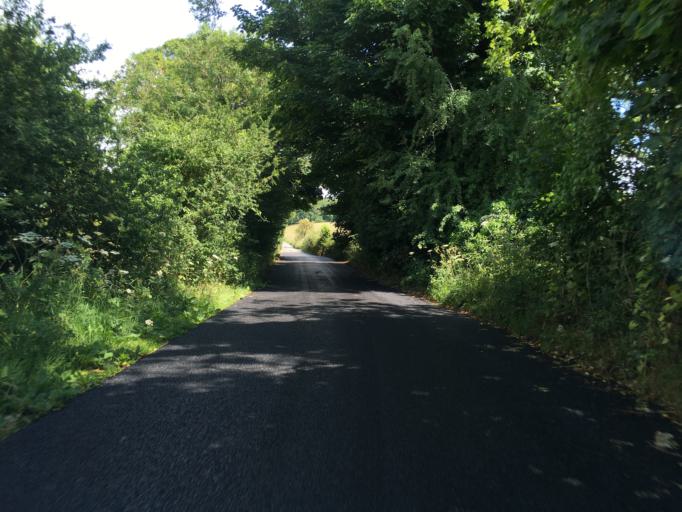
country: GB
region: England
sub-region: Gloucestershire
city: Tetbury
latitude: 51.6508
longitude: -2.1808
